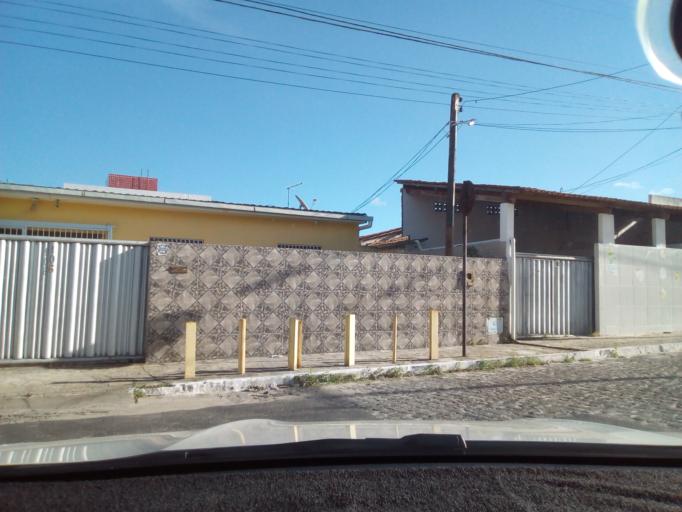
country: BR
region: Paraiba
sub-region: Joao Pessoa
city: Joao Pessoa
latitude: -7.1764
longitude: -34.8379
